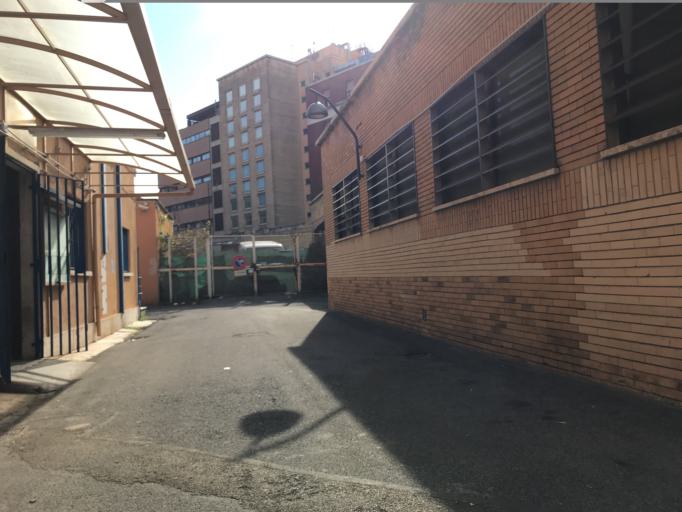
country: IT
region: Latium
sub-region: Citta metropolitana di Roma Capitale
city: Rome
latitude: 41.9013
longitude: 12.5131
